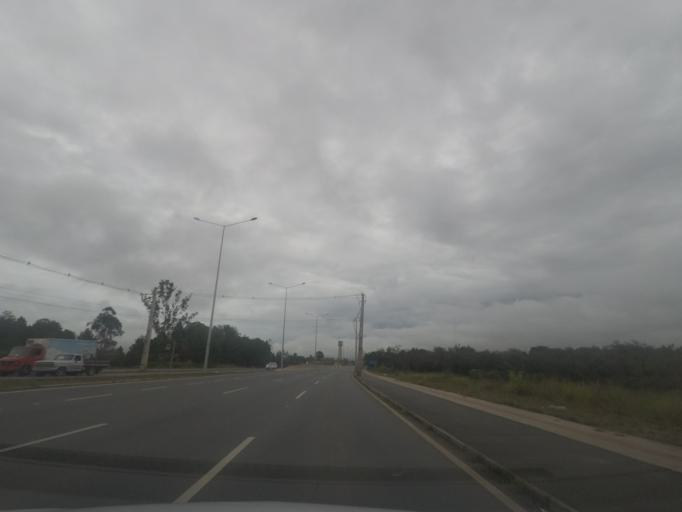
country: BR
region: Parana
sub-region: Piraquara
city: Piraquara
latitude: -25.4516
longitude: -49.1204
